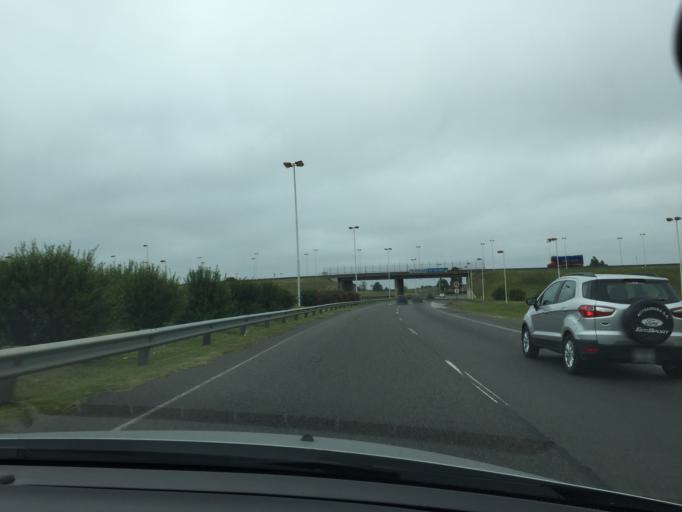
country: AR
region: Buenos Aires
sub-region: Partido de Ezeiza
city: Ezeiza
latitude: -34.8304
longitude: -58.5090
